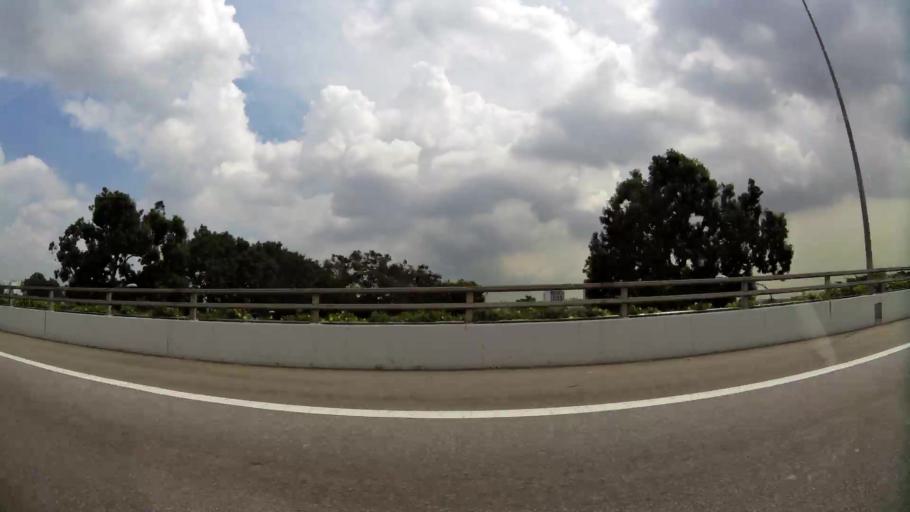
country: SG
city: Singapore
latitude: 1.3694
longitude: 103.8610
